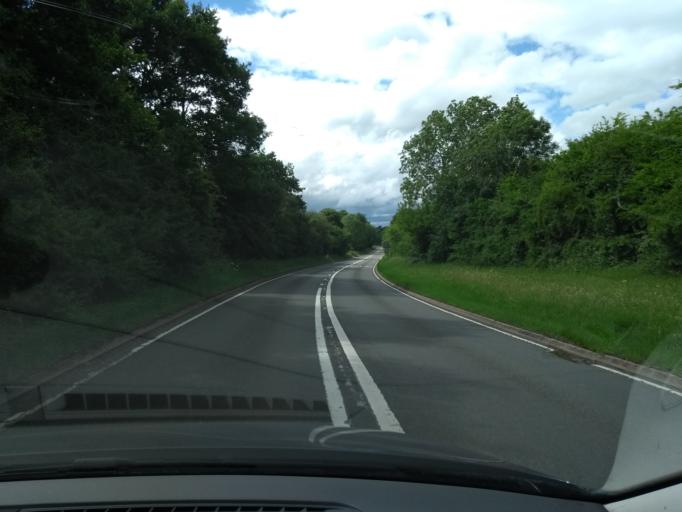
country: GB
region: England
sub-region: Warwickshire
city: Henley in Arden
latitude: 52.2846
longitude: -1.7377
